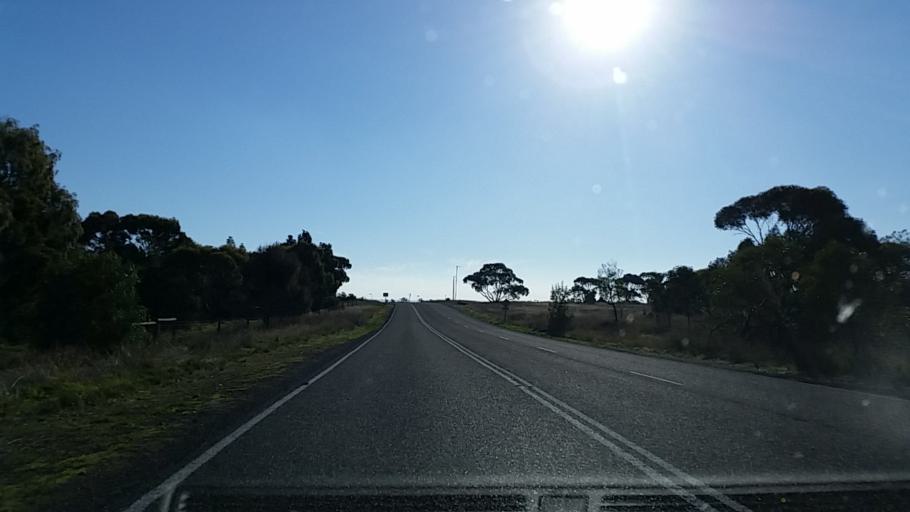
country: AU
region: South Australia
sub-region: Mount Barker
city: Callington
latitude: -35.1123
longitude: 139.0791
